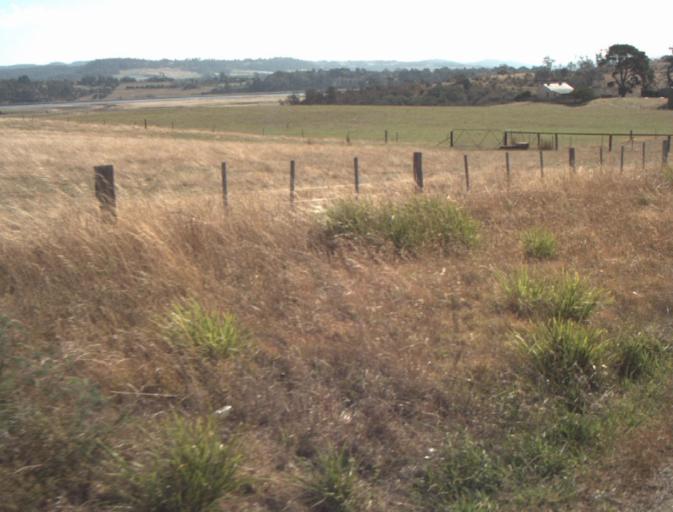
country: AU
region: Tasmania
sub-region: Launceston
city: Mayfield
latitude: -41.3522
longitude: 147.0999
